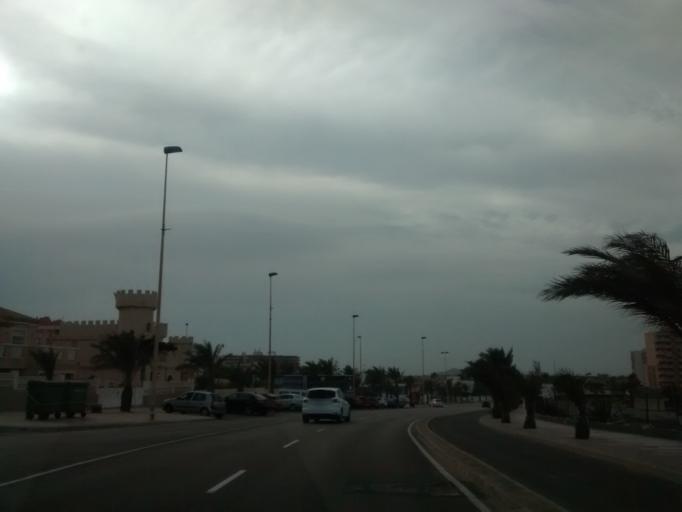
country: ES
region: Murcia
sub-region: Murcia
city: La Manga del Mar Menor
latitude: 37.6663
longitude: -0.7263
